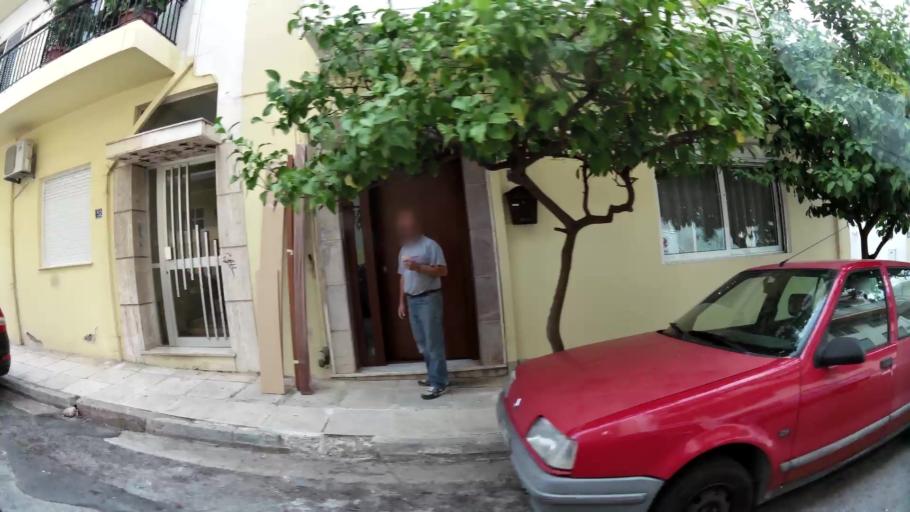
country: GR
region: Attica
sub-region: Nomarchia Athinas
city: Nea Filadelfeia
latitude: 38.0283
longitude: 23.7474
